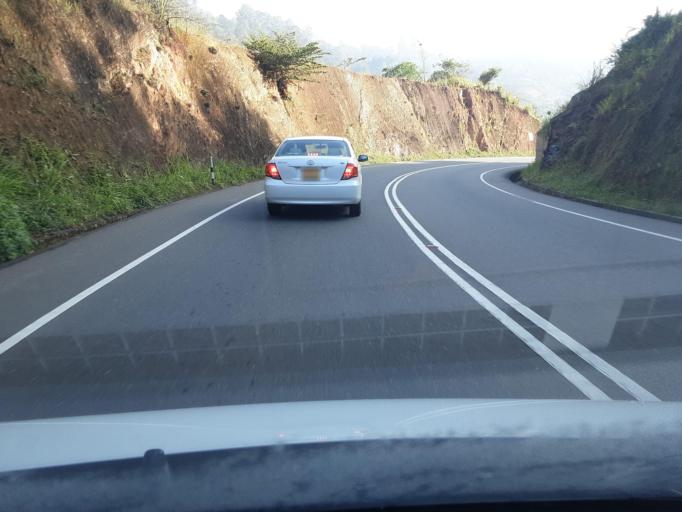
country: LK
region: Uva
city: Badulla
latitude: 6.9145
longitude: 80.9367
